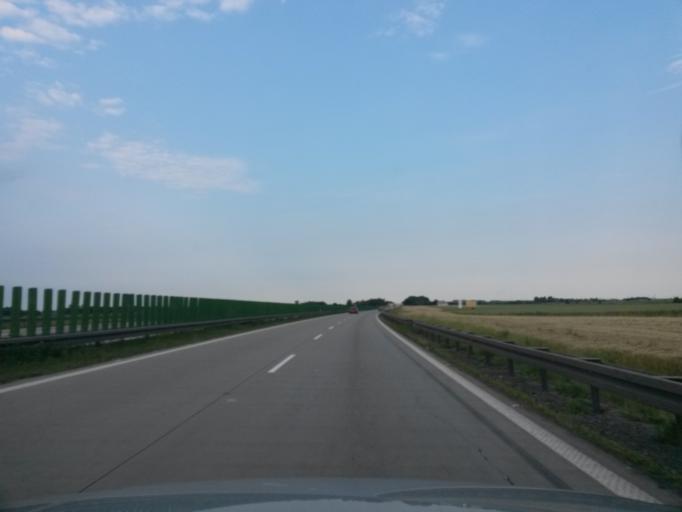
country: PL
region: Lower Silesian Voivodeship
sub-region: Powiat wroclawski
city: Katy Wroclawskie
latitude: 51.0349
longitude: 16.8102
